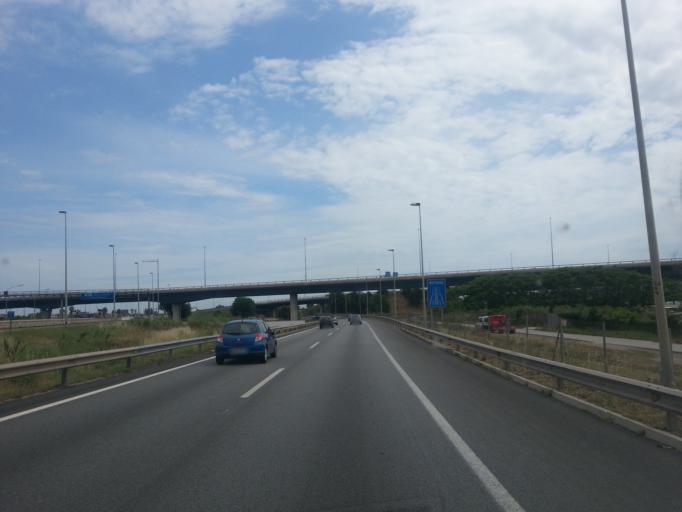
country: ES
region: Catalonia
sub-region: Provincia de Barcelona
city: Sant Feliu de Llobregat
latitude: 41.3793
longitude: 2.0306
